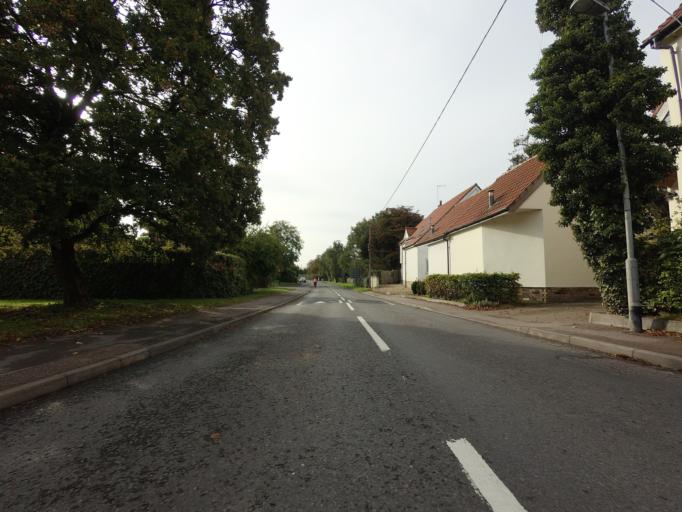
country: GB
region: England
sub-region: Cambridgeshire
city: Harston
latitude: 52.0919
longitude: 0.0723
